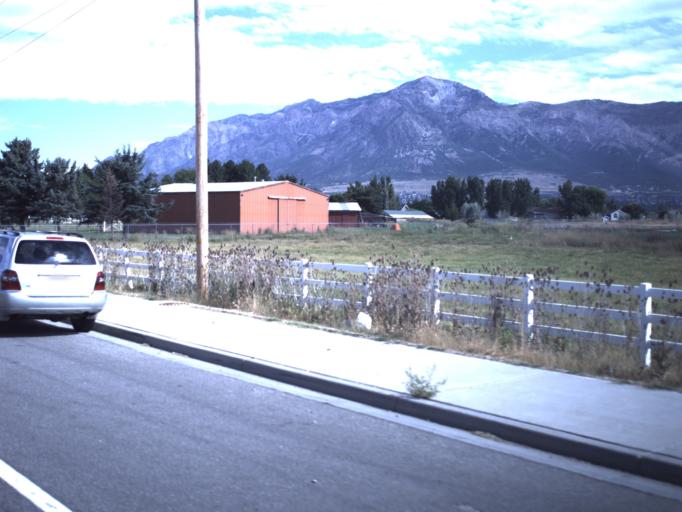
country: US
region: Utah
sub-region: Weber County
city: Harrisville
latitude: 41.2741
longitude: -111.9806
